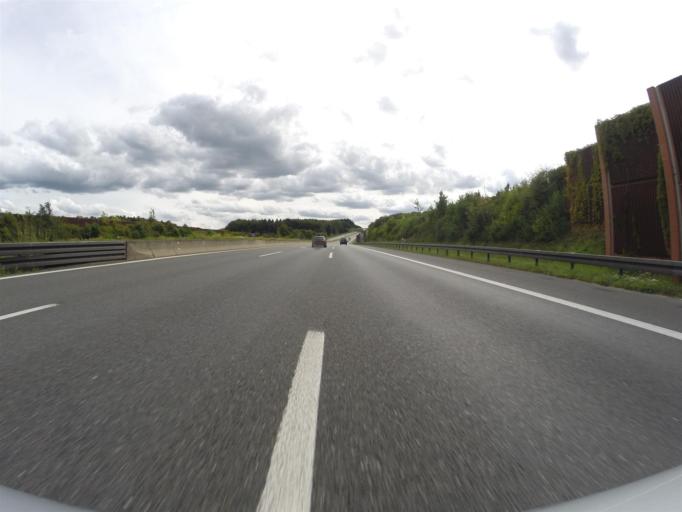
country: DE
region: Bavaria
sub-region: Regierungsbezirk Mittelfranken
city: Kirchensittenbach
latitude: 49.6334
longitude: 11.4230
